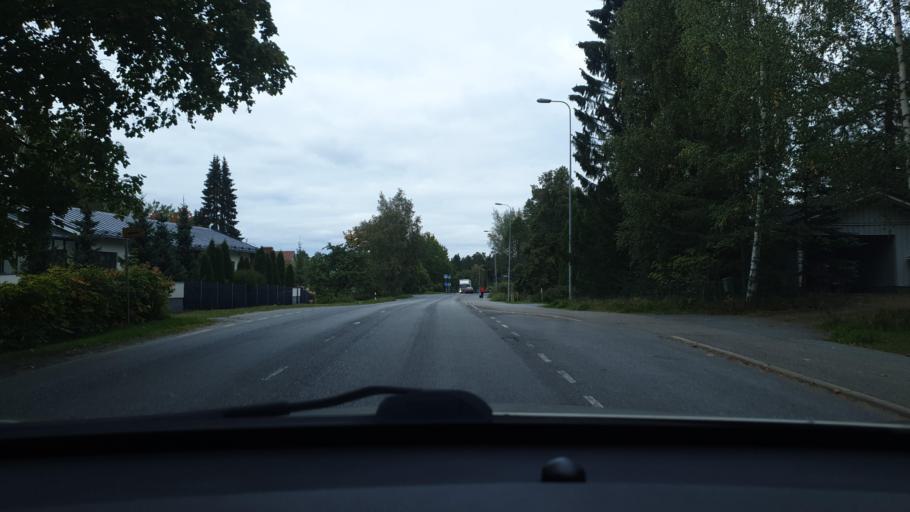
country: FI
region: Ostrobothnia
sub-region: Vaasa
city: Korsholm
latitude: 63.1016
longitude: 21.6748
